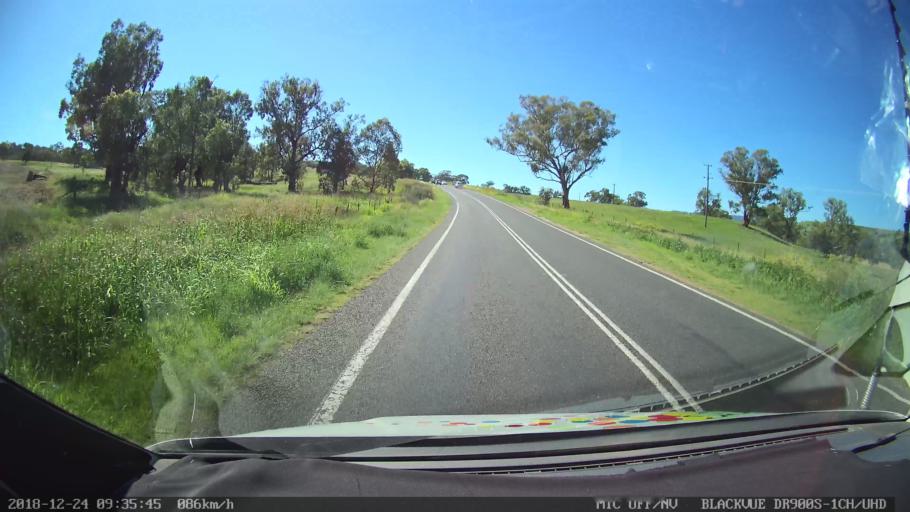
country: AU
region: New South Wales
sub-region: Liverpool Plains
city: Quirindi
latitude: -31.6333
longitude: 150.7194
